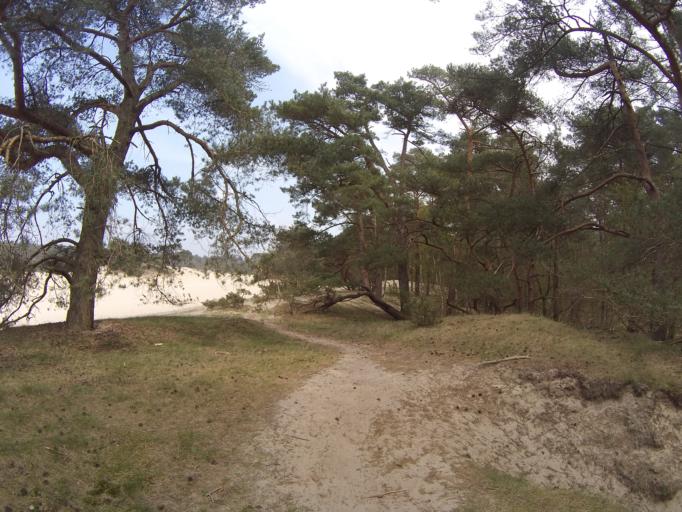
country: NL
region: Utrecht
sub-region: Gemeente Soest
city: Soest
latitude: 52.1496
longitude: 5.3164
